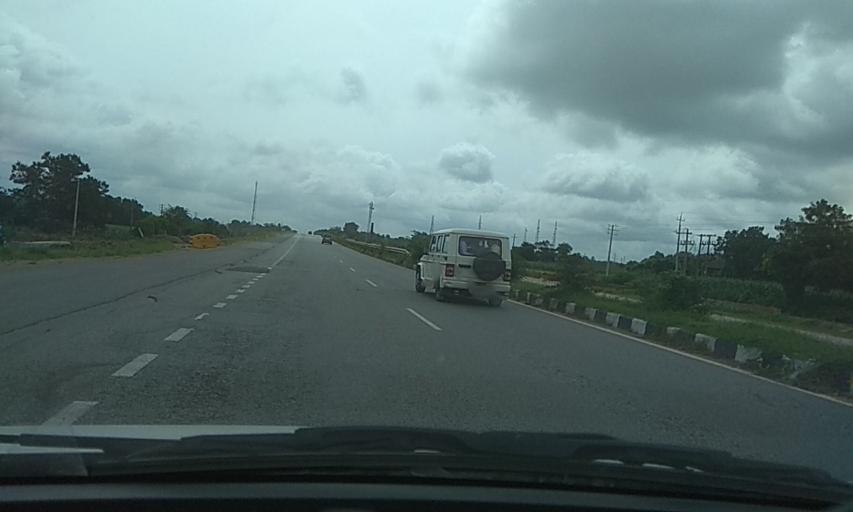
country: IN
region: Karnataka
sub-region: Davanagere
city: Mayakonda
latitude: 14.3957
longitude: 76.0349
